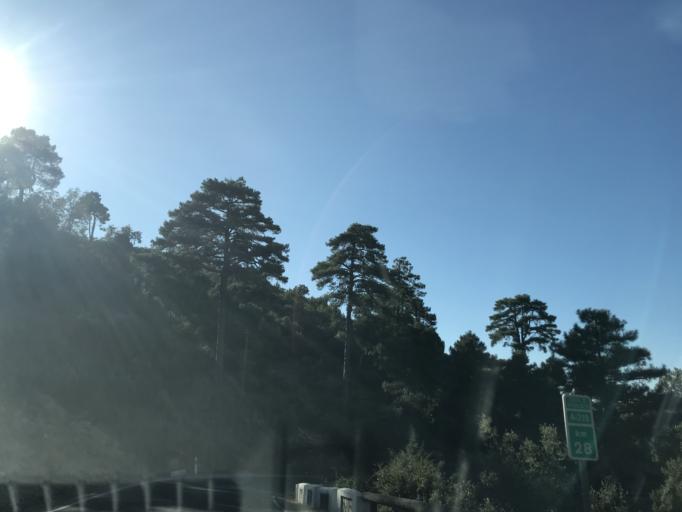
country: ES
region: Andalusia
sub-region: Provincia de Jaen
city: La Iruela
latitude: 37.9441
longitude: -2.9407
